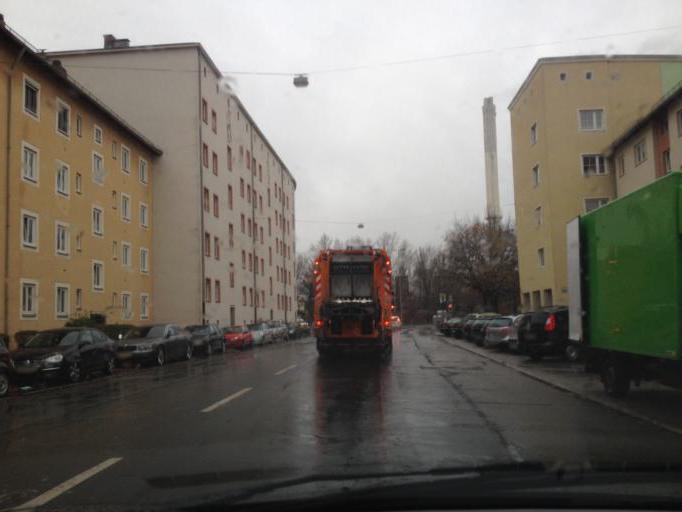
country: DE
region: Bavaria
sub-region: Regierungsbezirk Mittelfranken
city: Nuernberg
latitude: 49.4358
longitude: 11.0648
